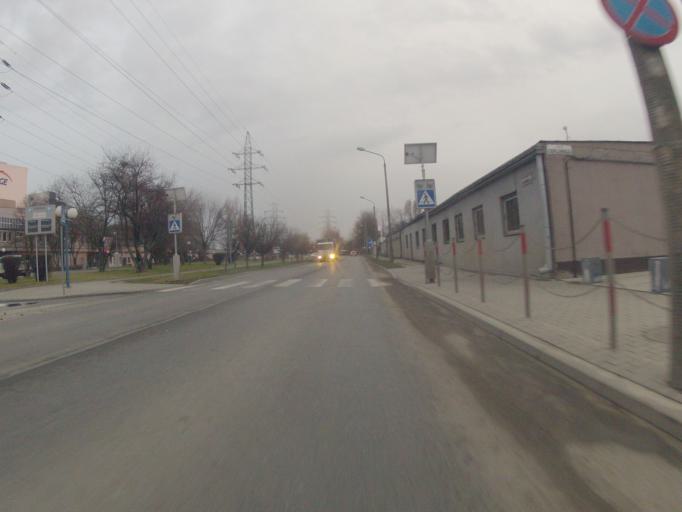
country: PL
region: Lesser Poland Voivodeship
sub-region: Krakow
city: Krakow
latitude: 50.0546
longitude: 20.0024
